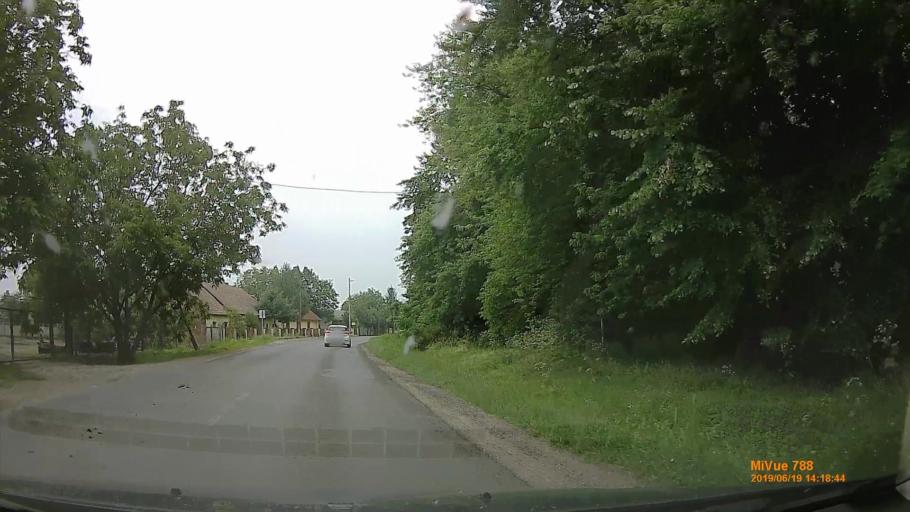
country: HU
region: Baranya
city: Szigetvar
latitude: 46.0395
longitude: 17.7823
